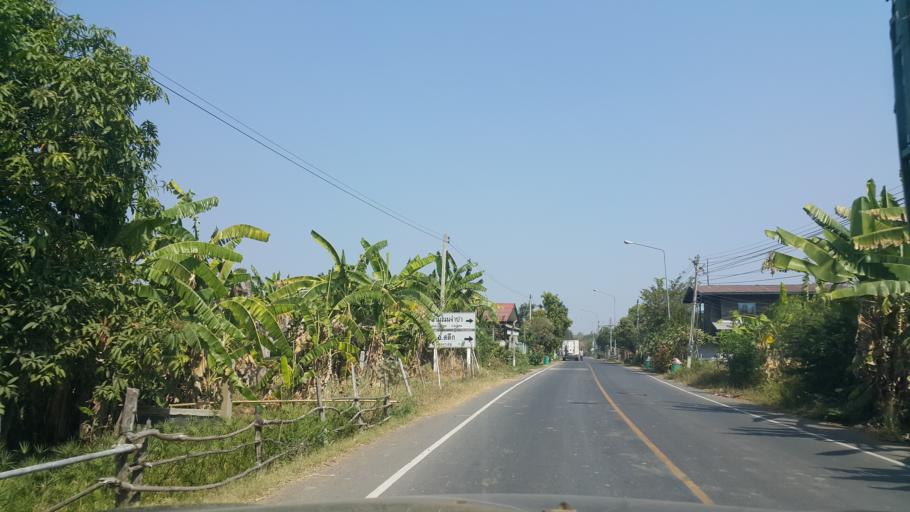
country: TH
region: Buriram
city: Satuek
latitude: 15.1294
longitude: 103.3760
